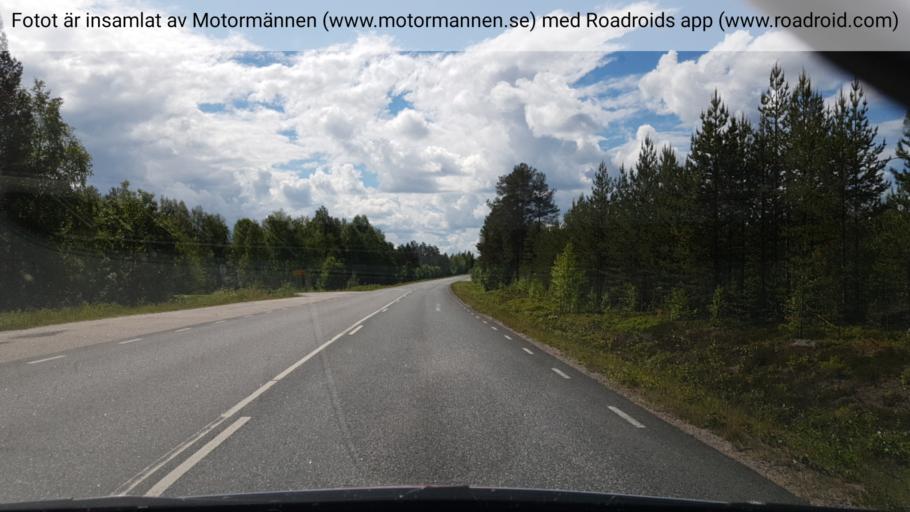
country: SE
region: Norrbotten
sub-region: Overtornea Kommun
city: OEvertornea
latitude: 66.3436
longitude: 23.6480
